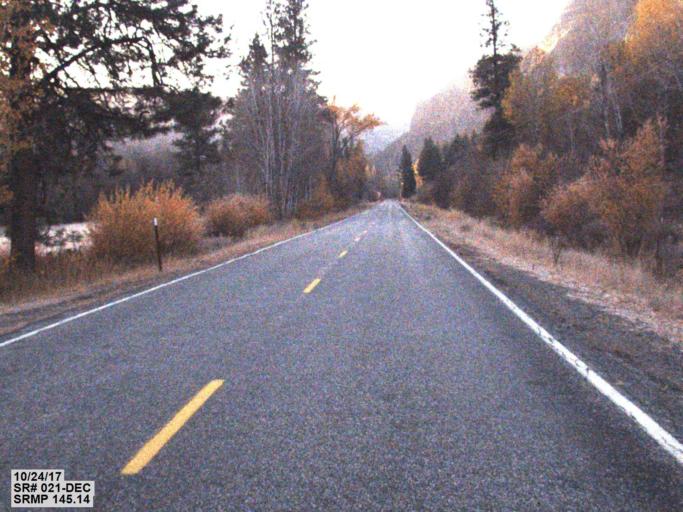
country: US
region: Washington
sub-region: Ferry County
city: Republic
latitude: 48.4523
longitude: -118.7468
